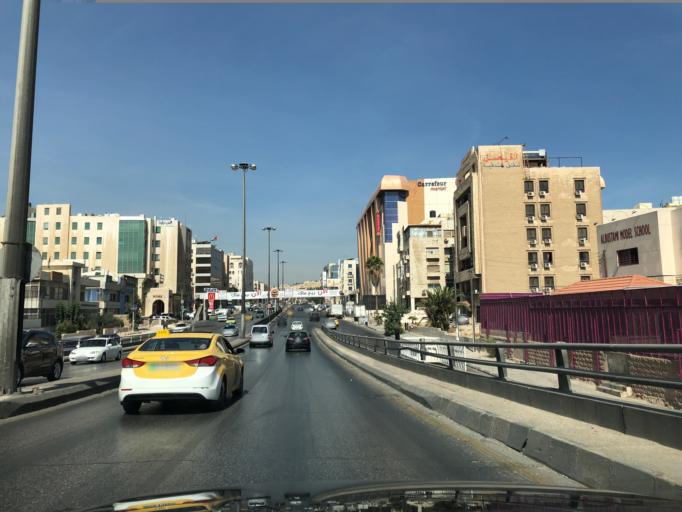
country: JO
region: Amman
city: Al Jubayhah
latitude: 31.9863
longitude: 35.8974
